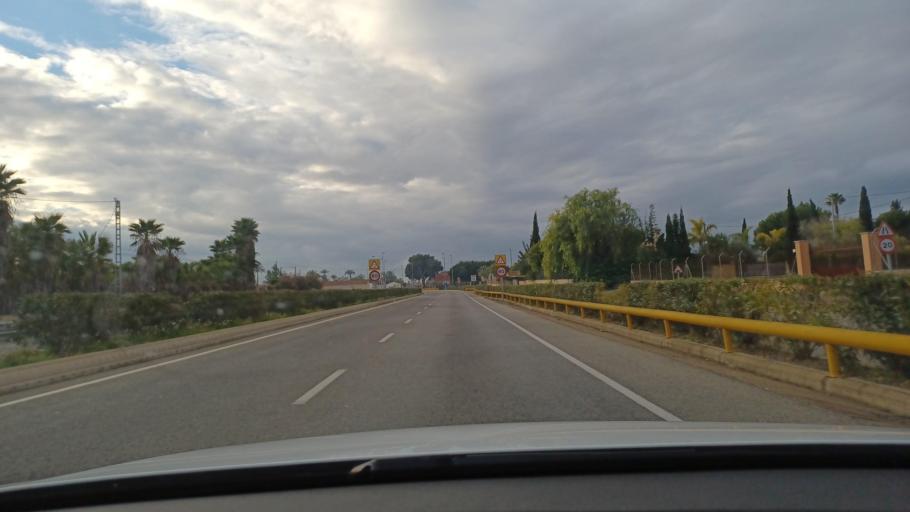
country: ES
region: Valencia
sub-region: Provincia de Alicante
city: Elche
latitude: 38.2176
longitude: -0.6973
